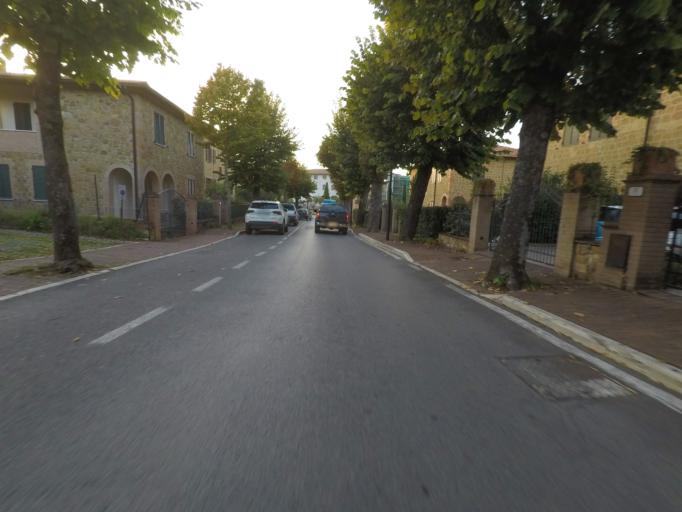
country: IT
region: Tuscany
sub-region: Provincia di Siena
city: Pienza
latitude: 43.0779
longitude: 11.6786
